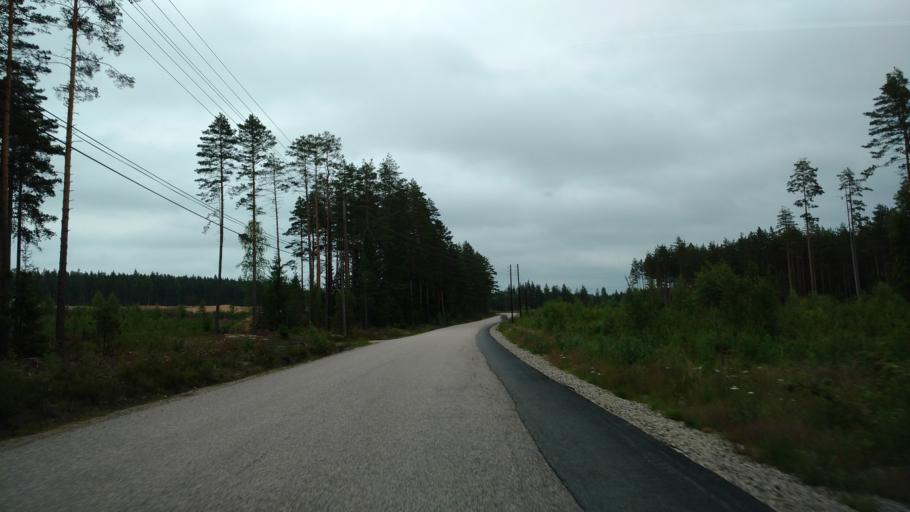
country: FI
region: Varsinais-Suomi
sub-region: Salo
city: Kiikala
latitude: 60.4340
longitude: 23.6030
